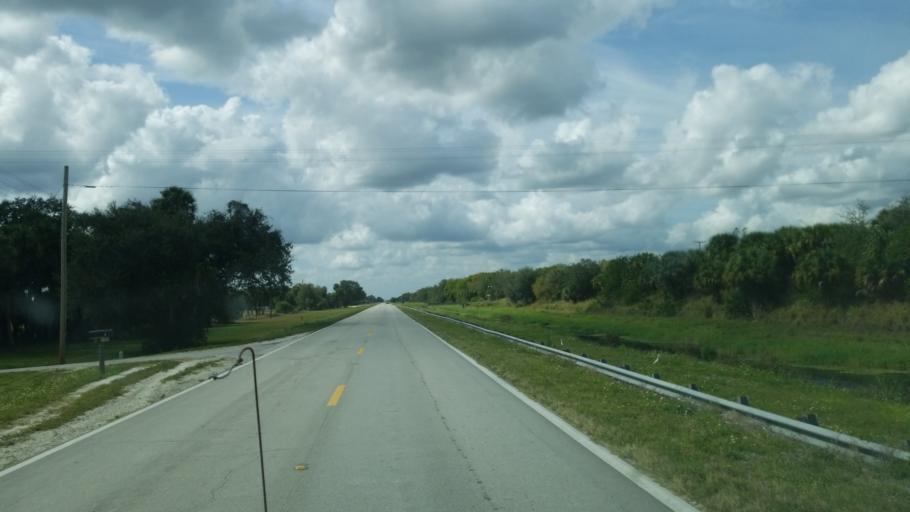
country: US
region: Florida
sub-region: Saint Lucie County
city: Lakewood Park
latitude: 27.4481
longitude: -80.5850
